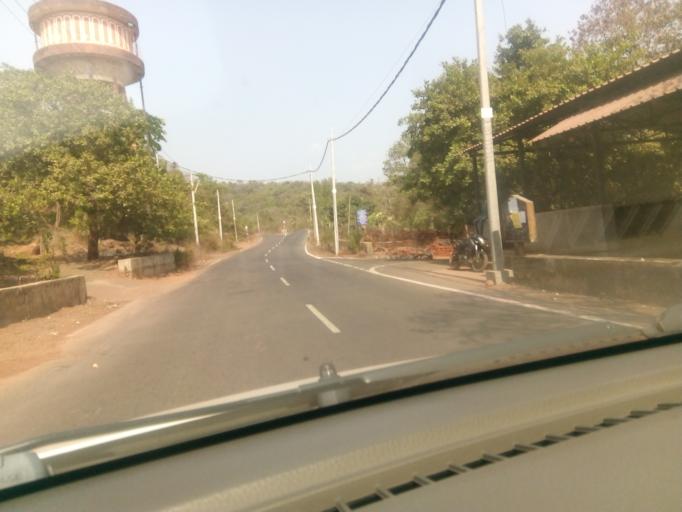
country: IN
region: Goa
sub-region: North Goa
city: Pernem
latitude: 15.6986
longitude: 73.8478
